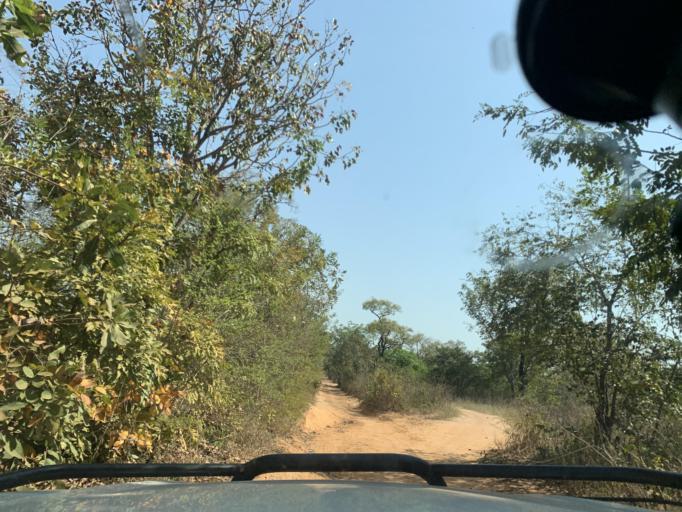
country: ML
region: Sikasso
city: Kolondieba
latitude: 10.8916
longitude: -6.7537
